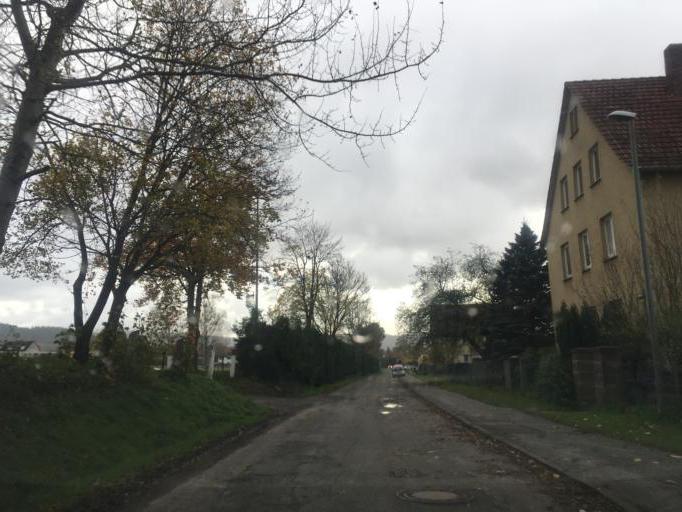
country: DE
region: Lower Saxony
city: Bodenfelde
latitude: 51.6449
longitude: 9.5600
